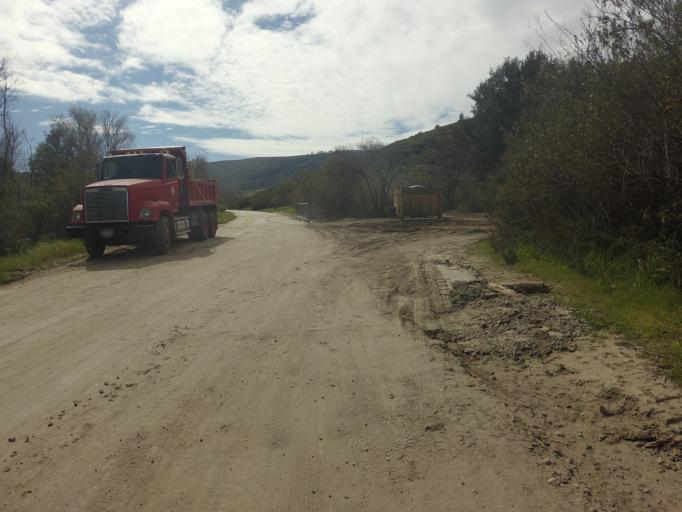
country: US
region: California
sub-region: Orange County
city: Aliso Viejo
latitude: 33.5413
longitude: -117.7375
